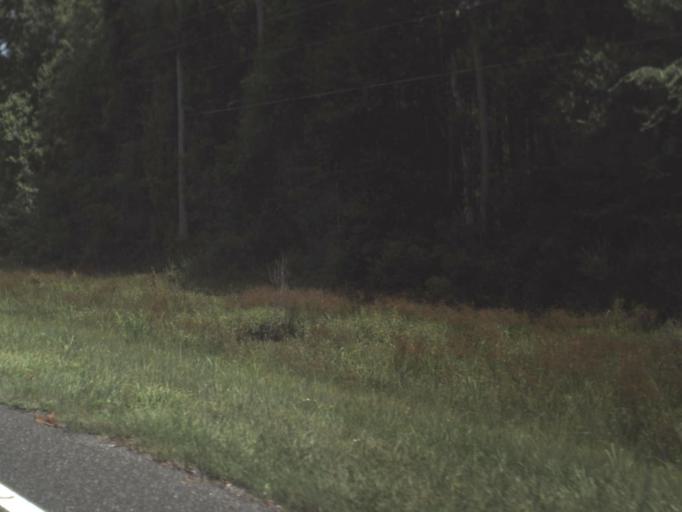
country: US
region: Florida
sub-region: Taylor County
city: Steinhatchee
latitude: 29.8830
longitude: -83.4101
